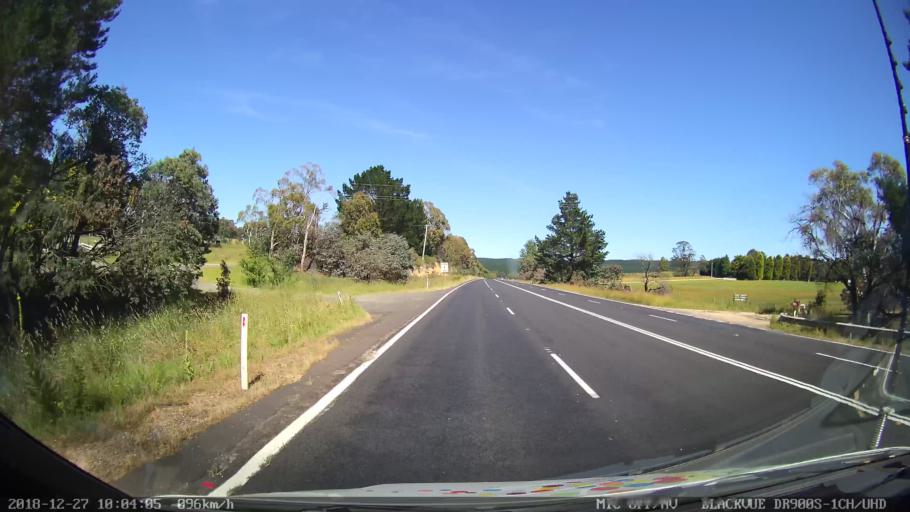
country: AU
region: New South Wales
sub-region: Lithgow
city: Portland
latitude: -33.4332
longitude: 149.8943
